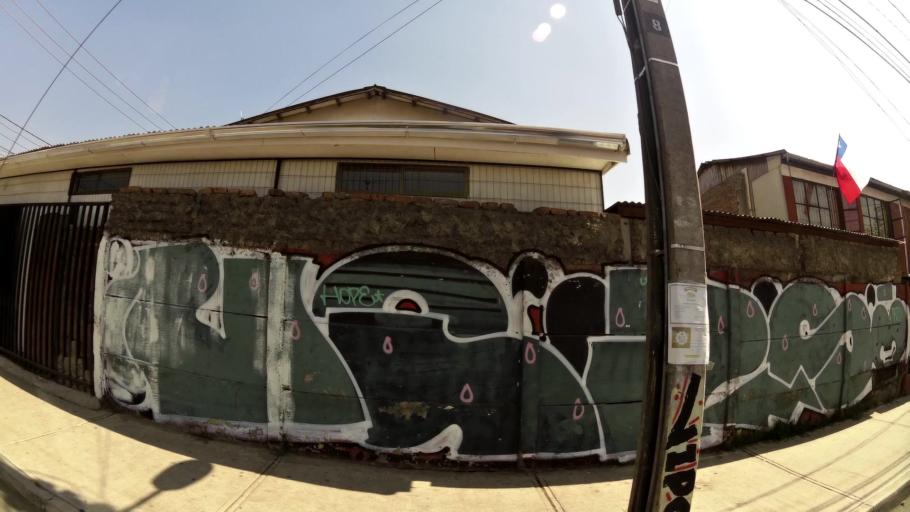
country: CL
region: Santiago Metropolitan
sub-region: Provincia de Santiago
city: La Pintana
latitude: -33.5487
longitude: -70.6161
